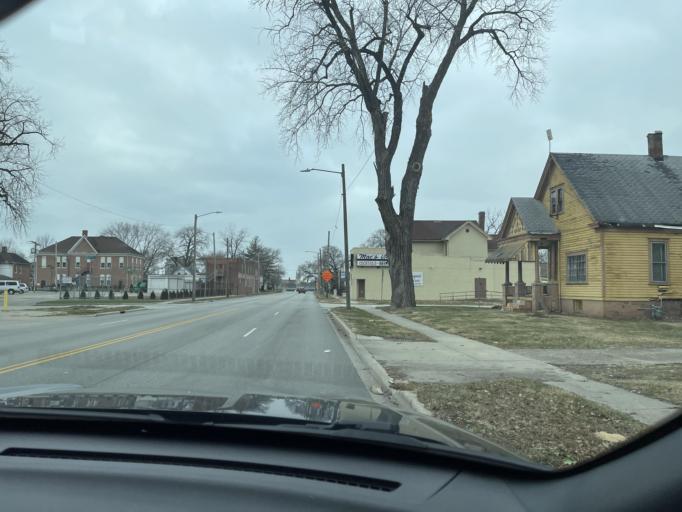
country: US
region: Illinois
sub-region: Sangamon County
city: Springfield
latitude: 39.7948
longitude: -89.6377
